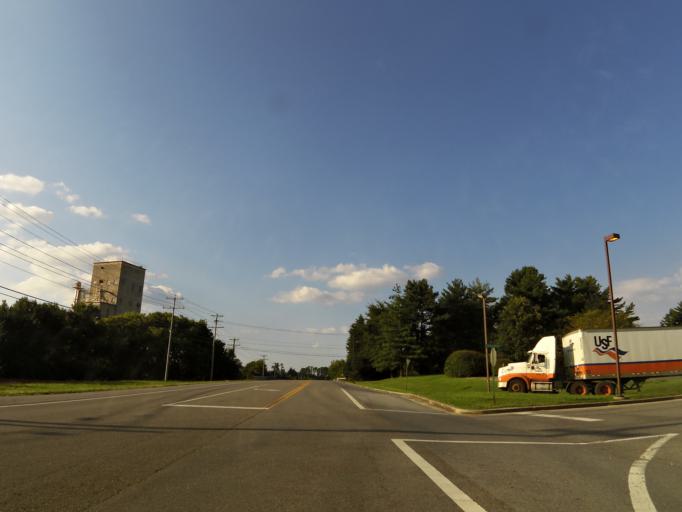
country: US
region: Tennessee
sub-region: Blount County
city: Eagleton Village
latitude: 35.8609
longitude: -83.9458
